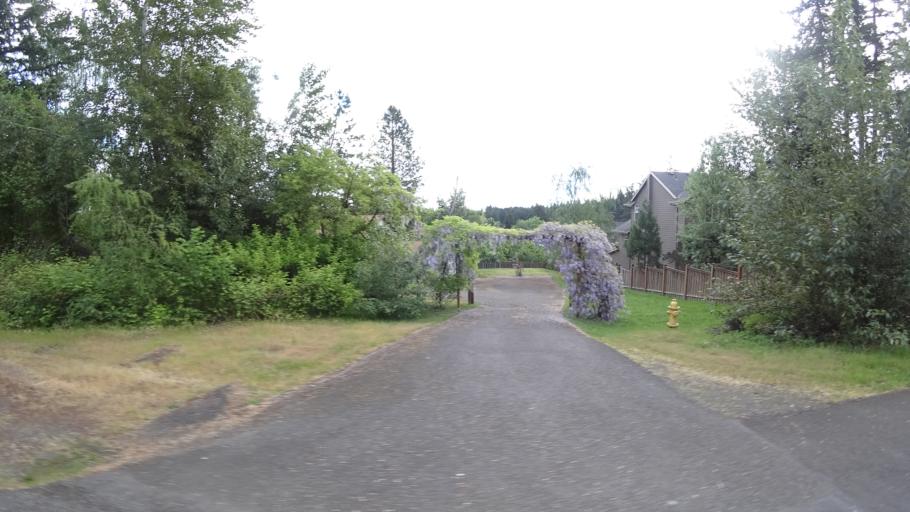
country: US
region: Oregon
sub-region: Washington County
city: Beaverton
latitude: 45.4703
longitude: -122.8366
